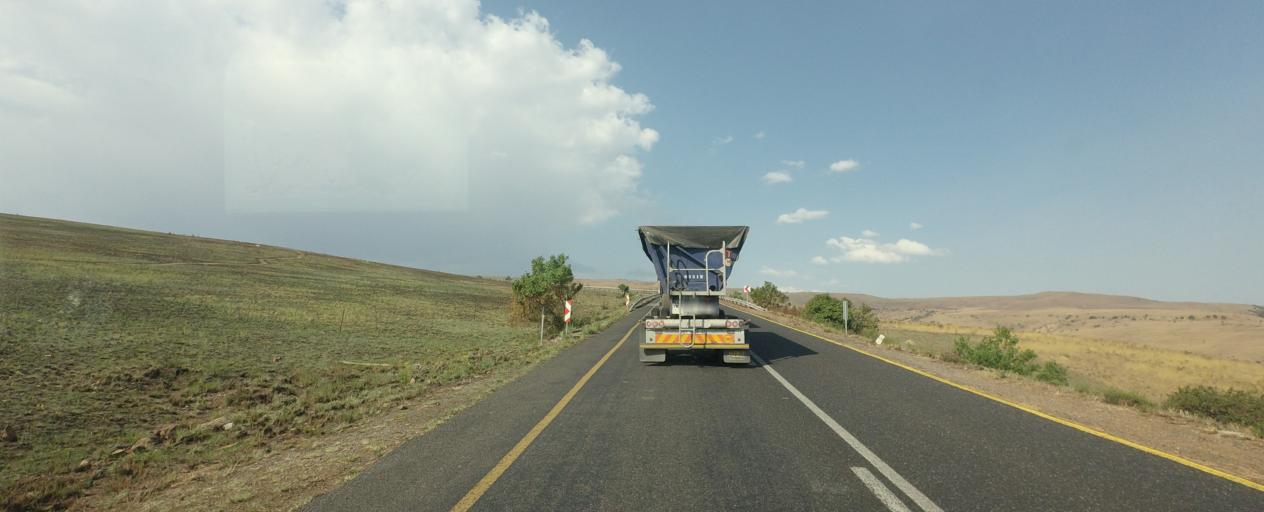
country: ZA
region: Mpumalanga
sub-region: Ehlanzeni District
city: Lydenburg
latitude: -25.1132
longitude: 30.5060
